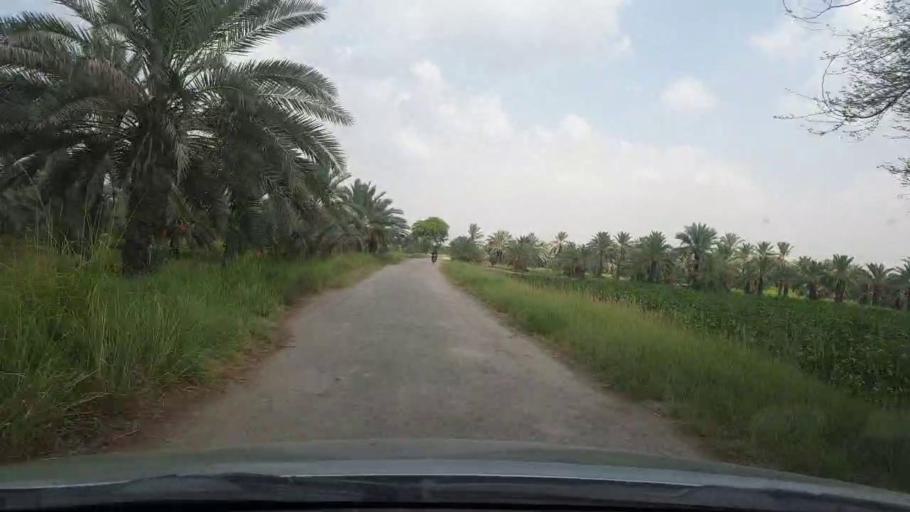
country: PK
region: Sindh
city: Khairpur
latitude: 27.4654
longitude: 68.7587
